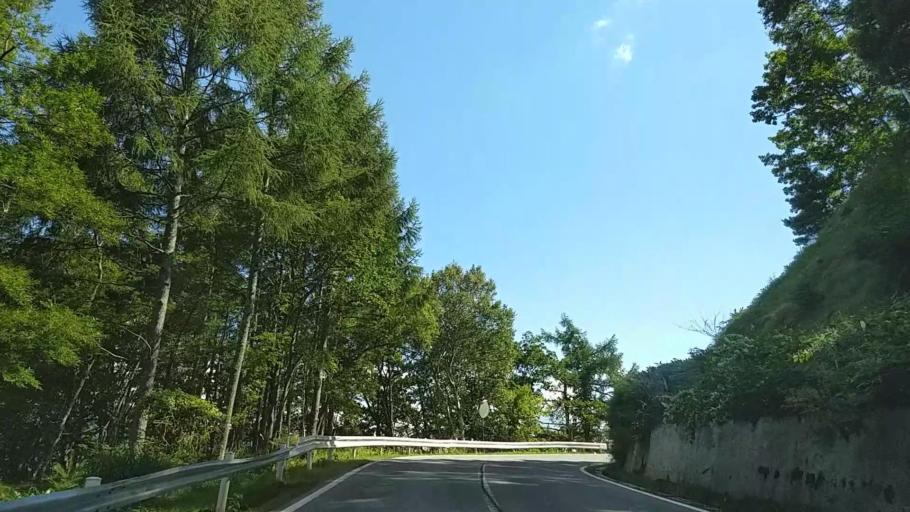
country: JP
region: Nagano
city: Chino
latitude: 36.0822
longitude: 138.2873
